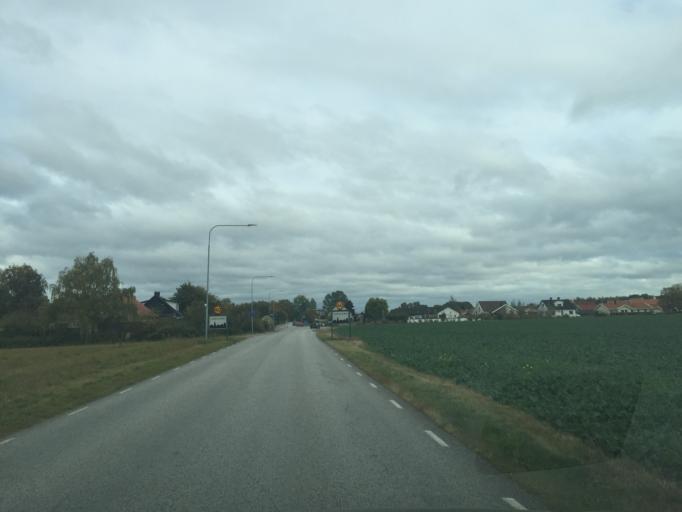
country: SE
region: Skane
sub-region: Kavlinge Kommun
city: Kaevlinge
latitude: 55.7674
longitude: 13.0728
